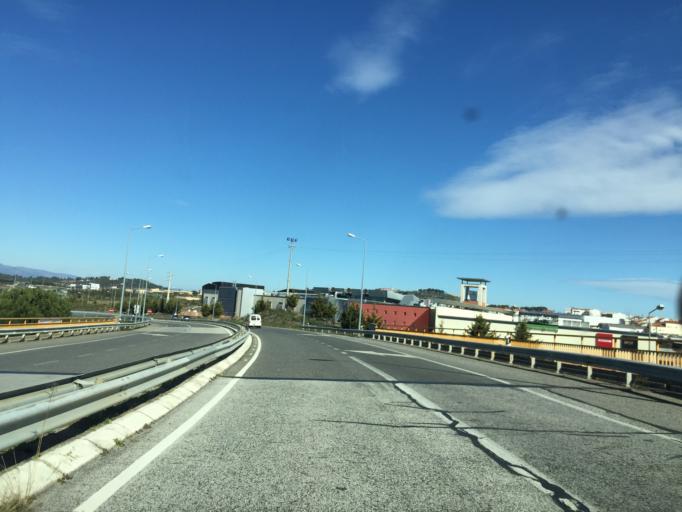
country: PT
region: Castelo Branco
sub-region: Castelo Branco
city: Castelo Branco
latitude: 39.8060
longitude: -7.5164
